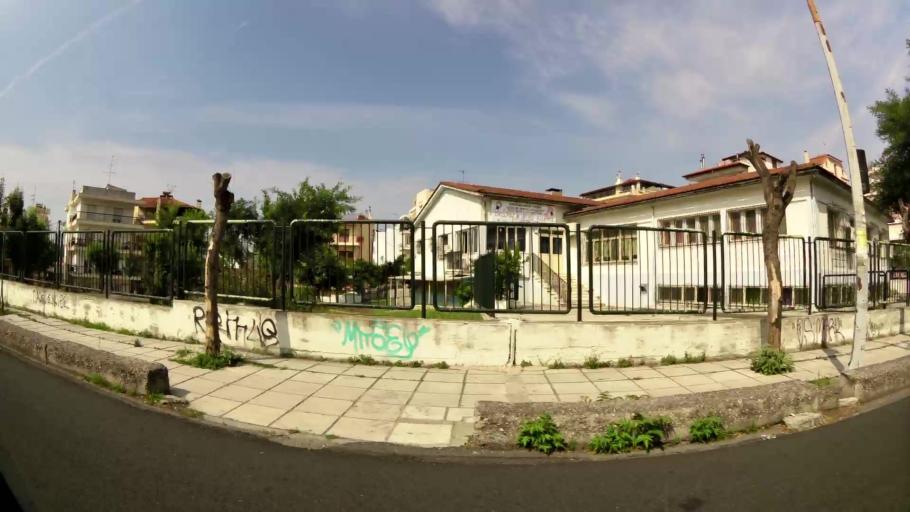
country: GR
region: Central Macedonia
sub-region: Nomos Thessalonikis
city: Agios Pavlos
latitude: 40.6484
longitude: 22.9600
